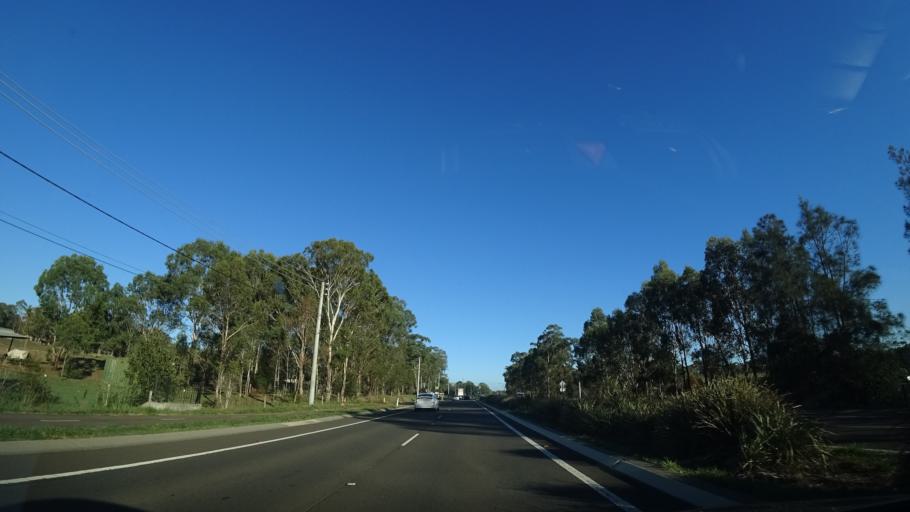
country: AU
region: New South Wales
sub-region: Blacktown
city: Riverstone
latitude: -33.6488
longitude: 150.8618
